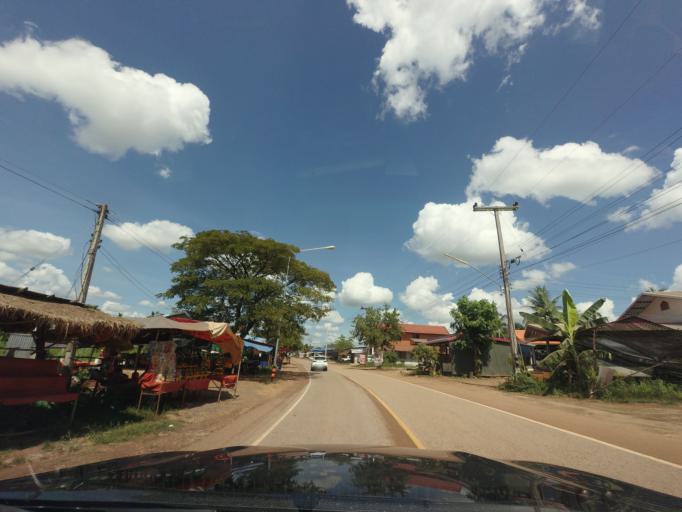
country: TH
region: Changwat Udon Thani
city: Ban Dung
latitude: 17.7410
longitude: 103.3575
